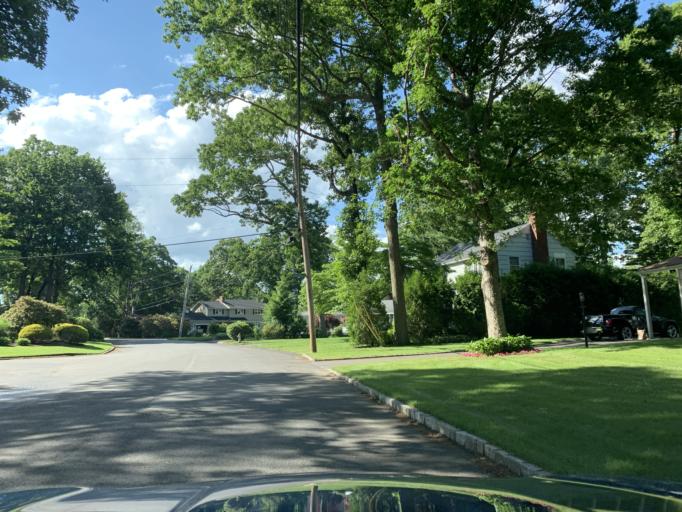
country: US
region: Rhode Island
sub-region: Kent County
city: East Greenwich
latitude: 41.6760
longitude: -71.4593
